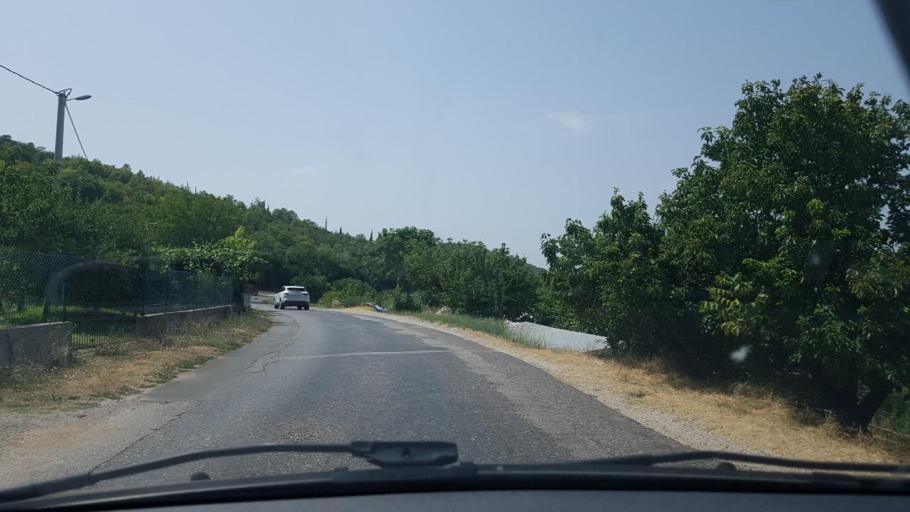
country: BA
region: Federation of Bosnia and Herzegovina
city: Tasovcici
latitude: 43.0212
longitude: 17.7647
